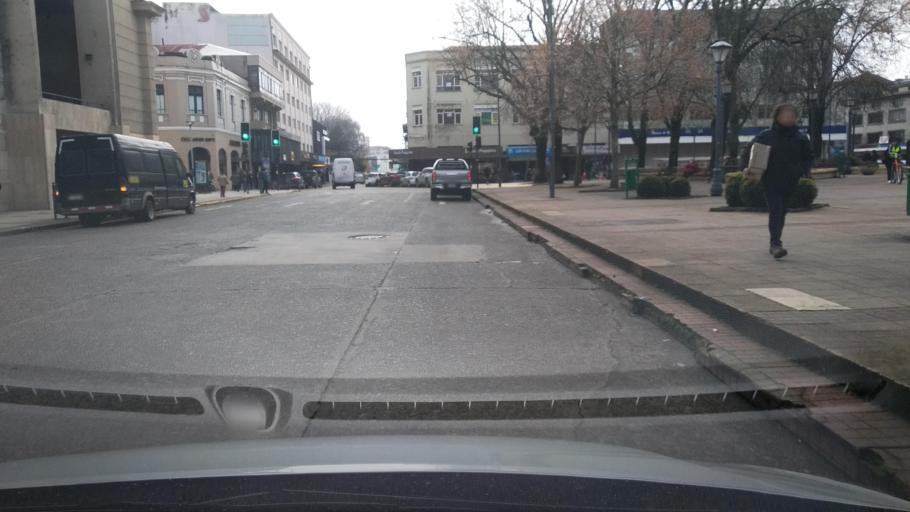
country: CL
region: Los Rios
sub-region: Provincia de Valdivia
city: Valdivia
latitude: -39.8144
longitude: -73.2462
